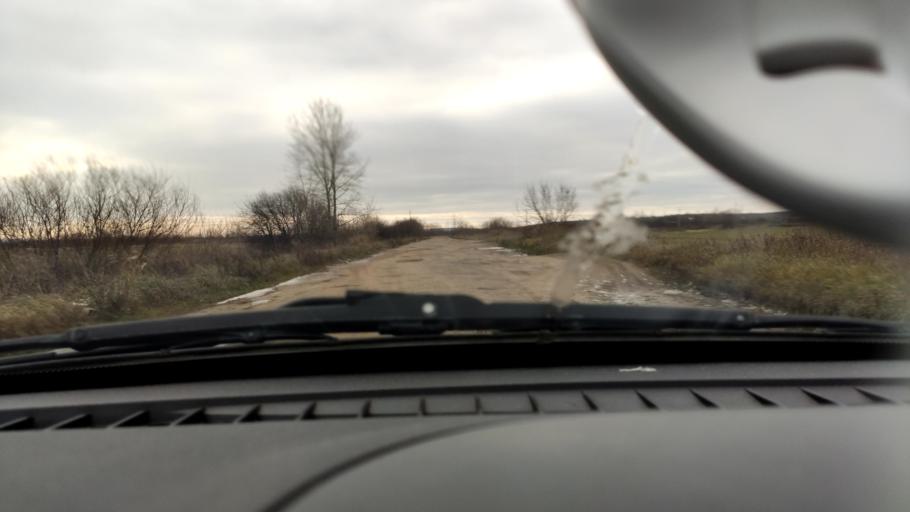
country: RU
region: Perm
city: Kondratovo
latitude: 57.9876
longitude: 56.0869
